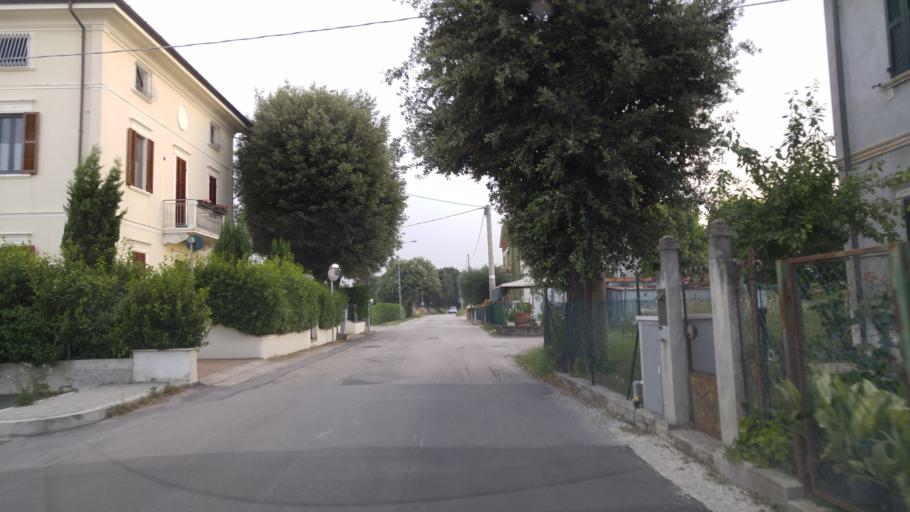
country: IT
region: The Marches
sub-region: Provincia di Pesaro e Urbino
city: Rosciano
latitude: 43.8289
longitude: 13.0030
